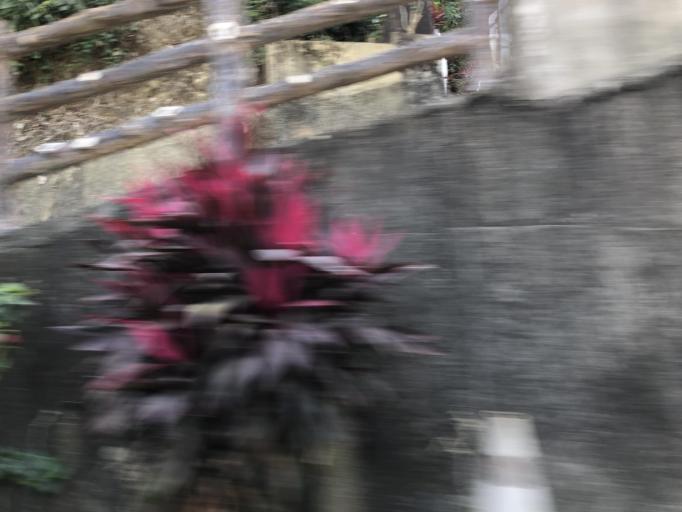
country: TW
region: Taiwan
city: Yujing
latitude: 23.0160
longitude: 120.3841
